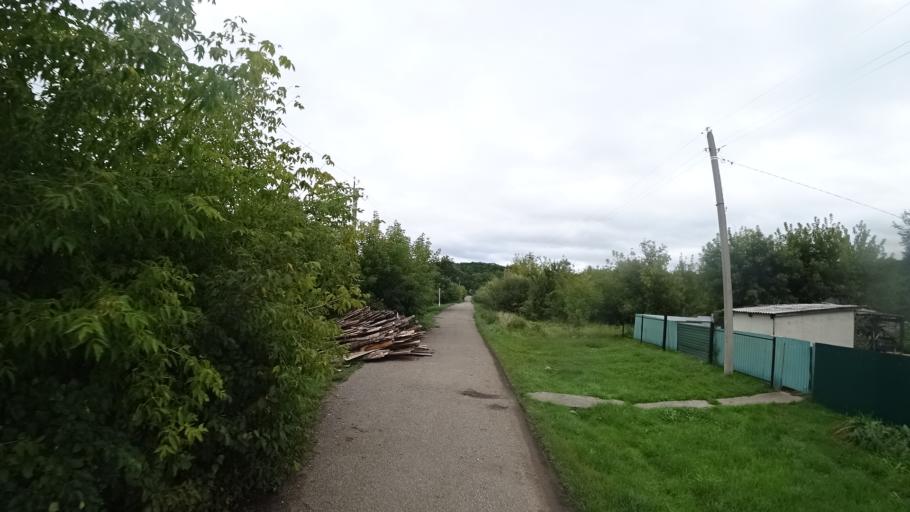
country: RU
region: Primorskiy
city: Chernigovka
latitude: 44.4541
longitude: 132.5929
